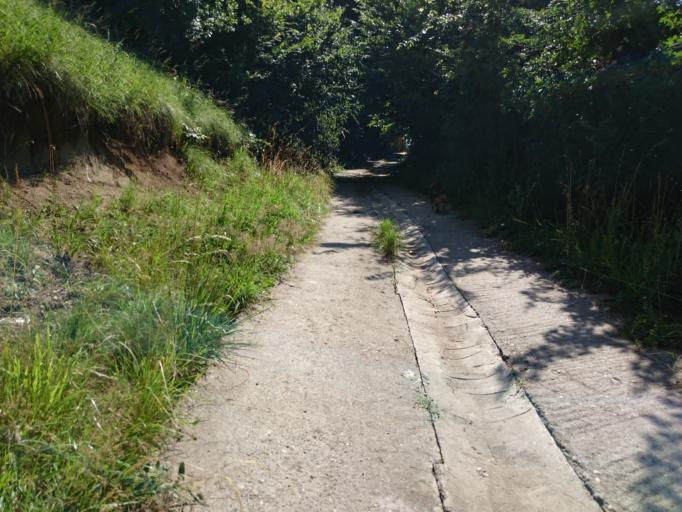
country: RO
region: Mures
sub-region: Municipiul Sighisoara
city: Sighisoara
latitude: 46.2150
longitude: 24.7980
